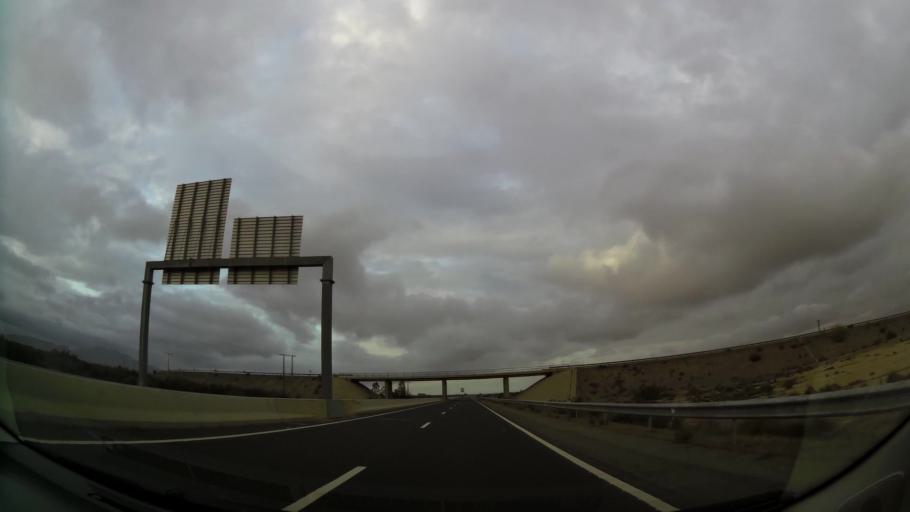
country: MA
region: Taza-Al Hoceima-Taounate
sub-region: Taza
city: Guercif
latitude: 34.3545
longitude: -3.3064
